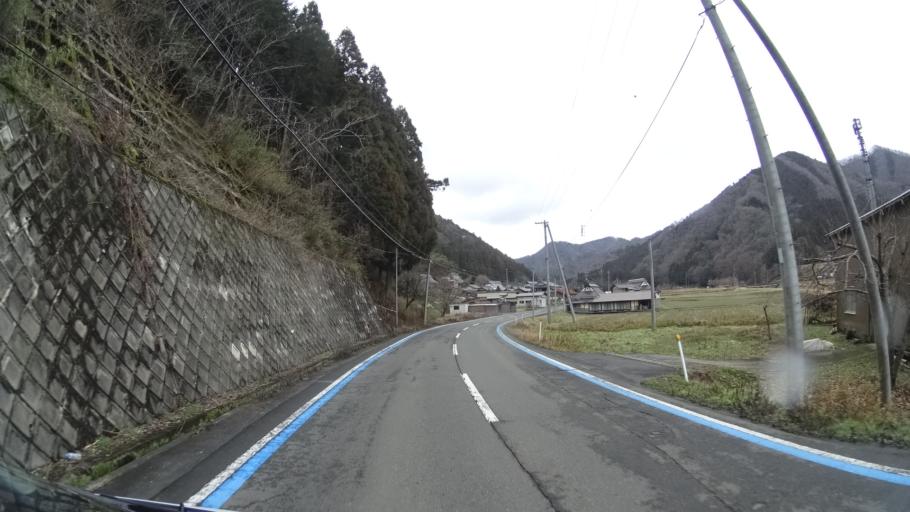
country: JP
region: Kyoto
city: Maizuru
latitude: 35.3952
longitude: 135.4131
